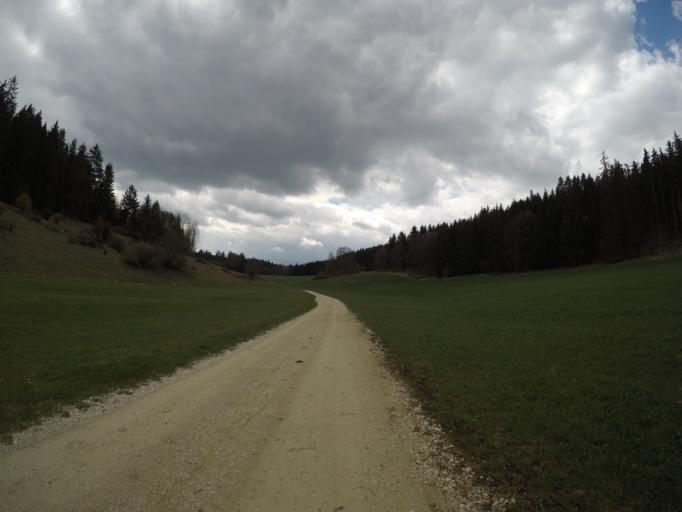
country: DE
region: Baden-Wuerttemberg
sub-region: Tuebingen Region
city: Nellingen
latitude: 48.5058
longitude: 9.7939
